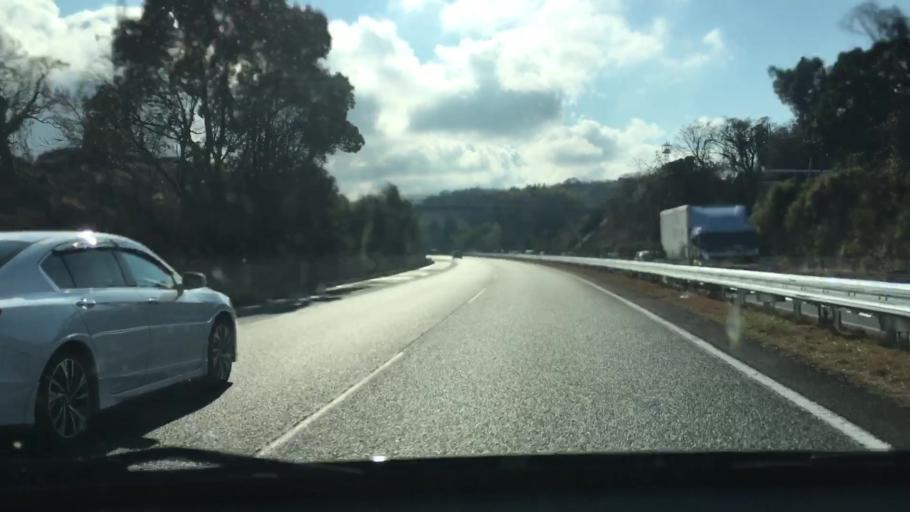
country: JP
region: Kumamoto
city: Matsubase
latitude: 32.5613
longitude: 130.6981
